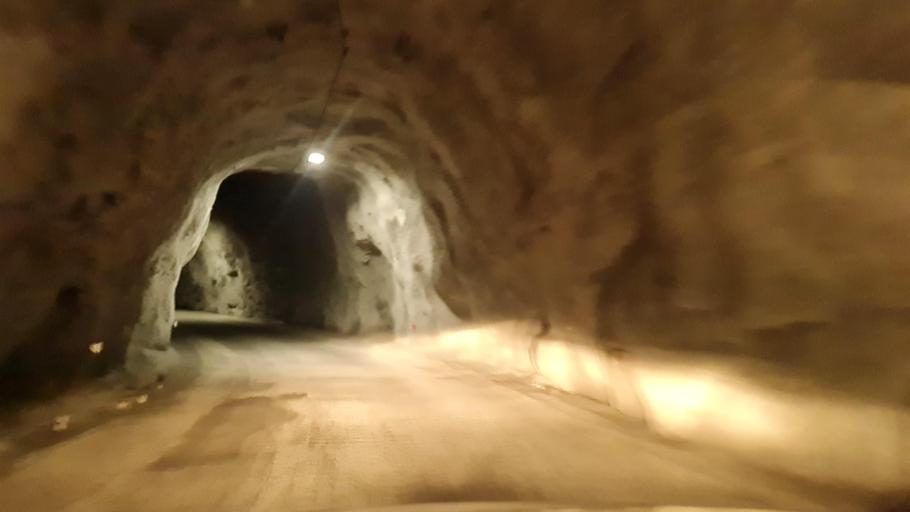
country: IT
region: Piedmont
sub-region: Provincia Verbano-Cusio-Ossola
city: Baceno
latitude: 46.3012
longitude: 8.2694
